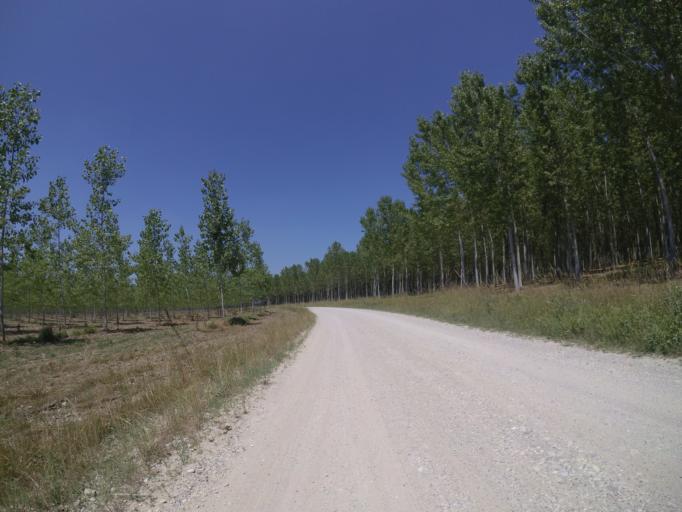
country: IT
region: Friuli Venezia Giulia
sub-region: Provincia di Udine
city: Bertiolo
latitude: 45.9196
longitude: 13.0268
